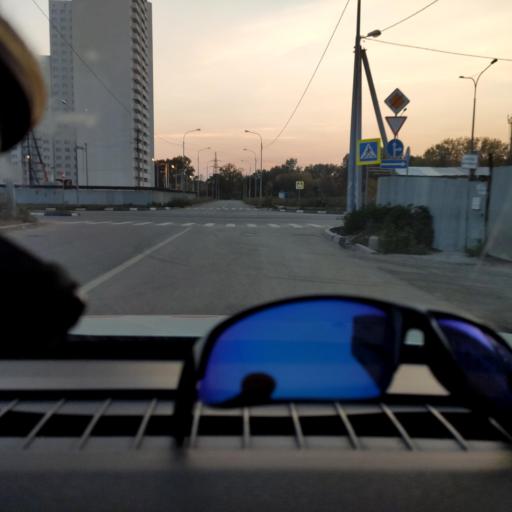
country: RU
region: Samara
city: Samara
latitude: 53.1463
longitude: 50.0765
